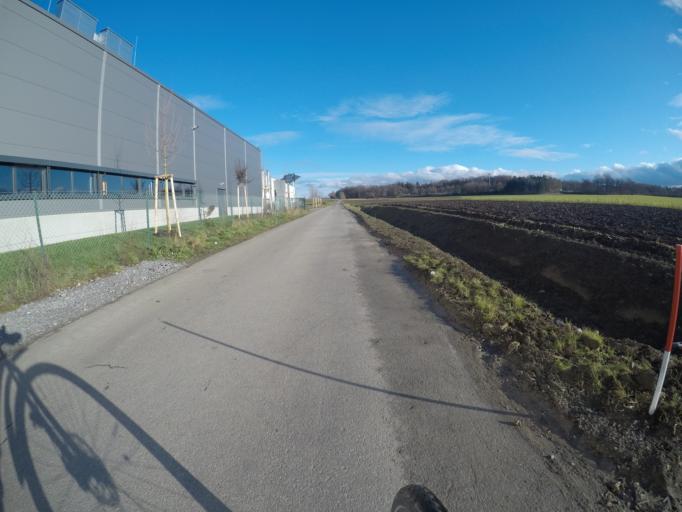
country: DE
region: Baden-Wuerttemberg
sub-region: Regierungsbezirk Stuttgart
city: Bondorf
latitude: 48.5272
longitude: 8.8801
